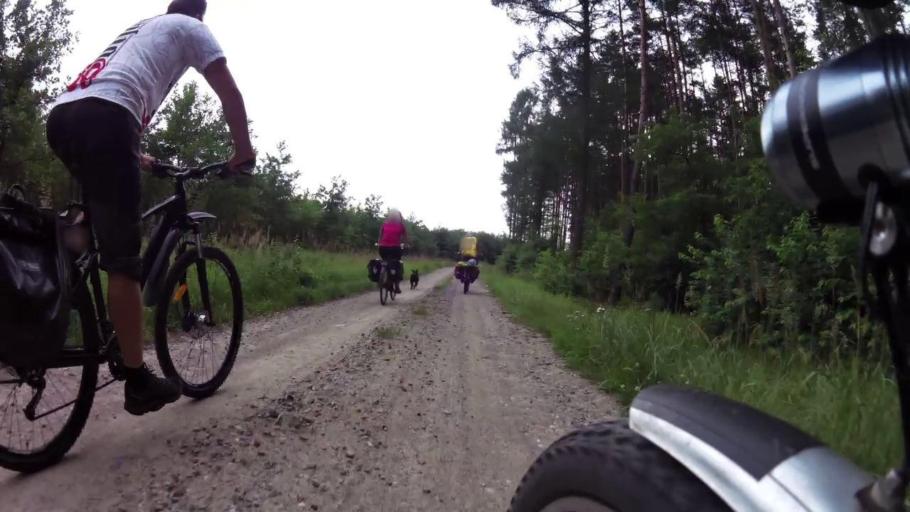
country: PL
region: West Pomeranian Voivodeship
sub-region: Powiat gryfinski
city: Mieszkowice
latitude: 52.8277
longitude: 14.5861
